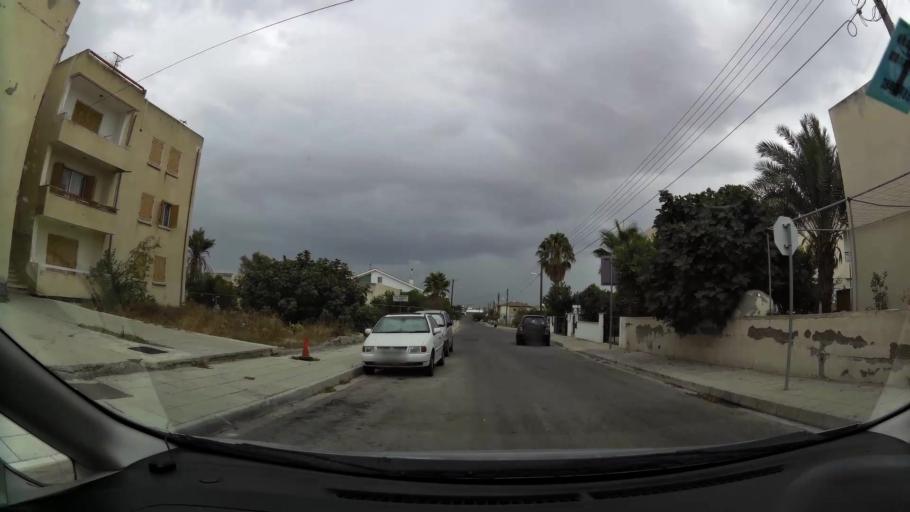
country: CY
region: Lefkosia
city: Geri
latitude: 35.1126
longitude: 33.3894
